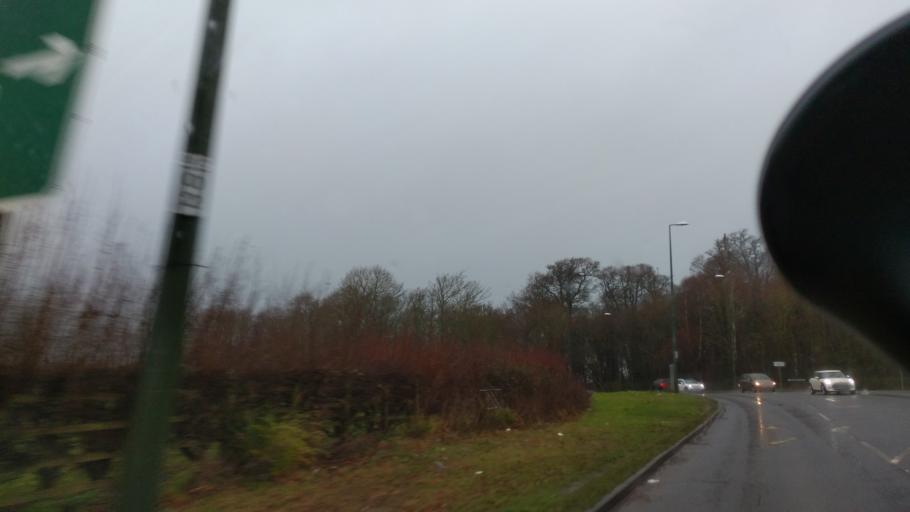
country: GB
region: England
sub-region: West Sussex
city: Arundel
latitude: 50.8455
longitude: -0.5407
